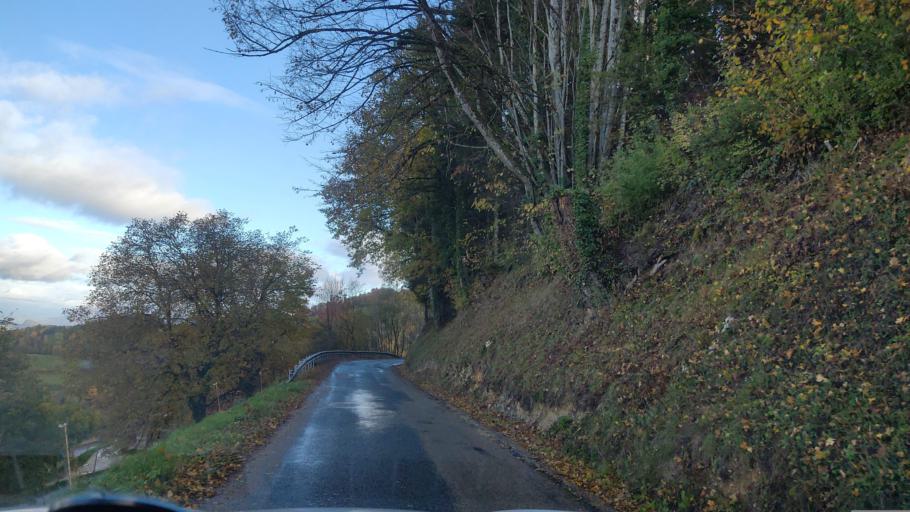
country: FR
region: Rhone-Alpes
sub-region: Departement de la Savoie
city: Novalaise
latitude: 45.6313
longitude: 5.7888
